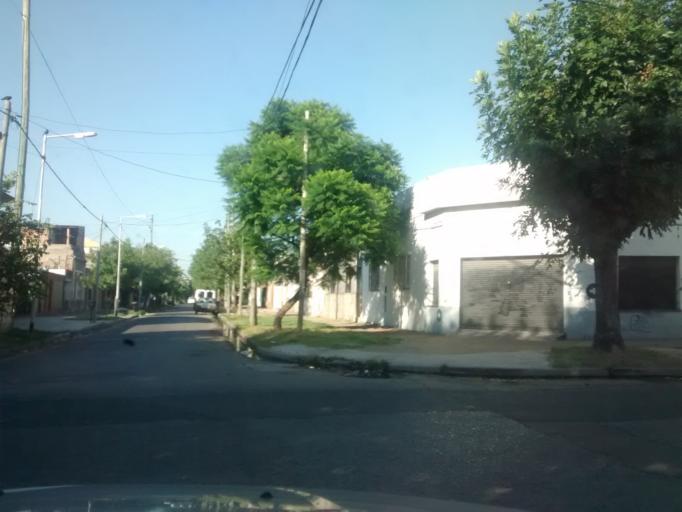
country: AR
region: Buenos Aires
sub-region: Partido de Avellaneda
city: Avellaneda
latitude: -34.6840
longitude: -58.3533
